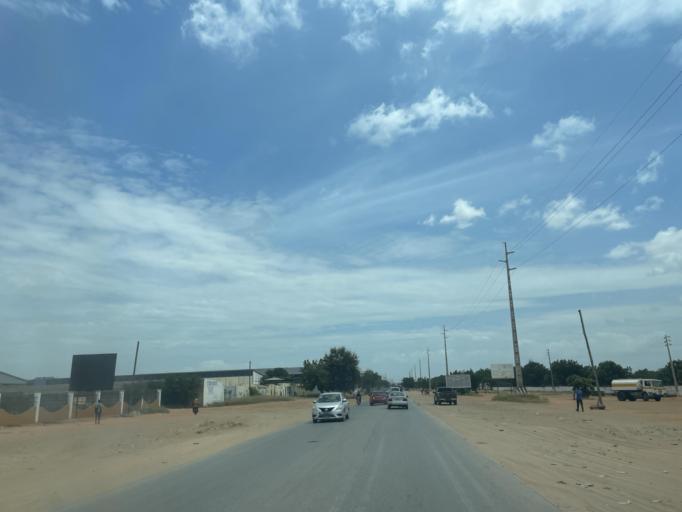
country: AO
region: Luanda
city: Luanda
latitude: -8.9396
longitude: 13.3832
